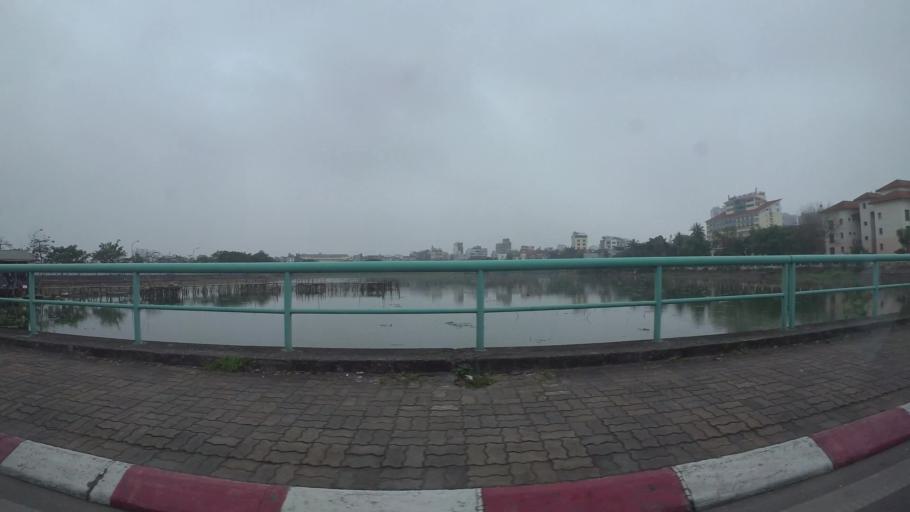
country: VN
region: Ha Noi
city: Tay Ho
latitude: 21.0679
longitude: 105.8190
